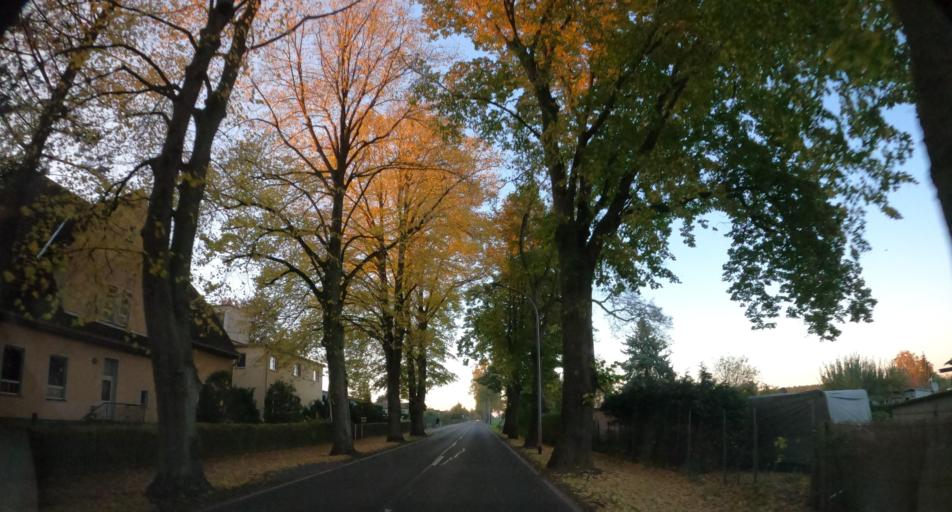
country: DE
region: Mecklenburg-Vorpommern
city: Ueckermunde
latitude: 53.7427
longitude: 14.0335
